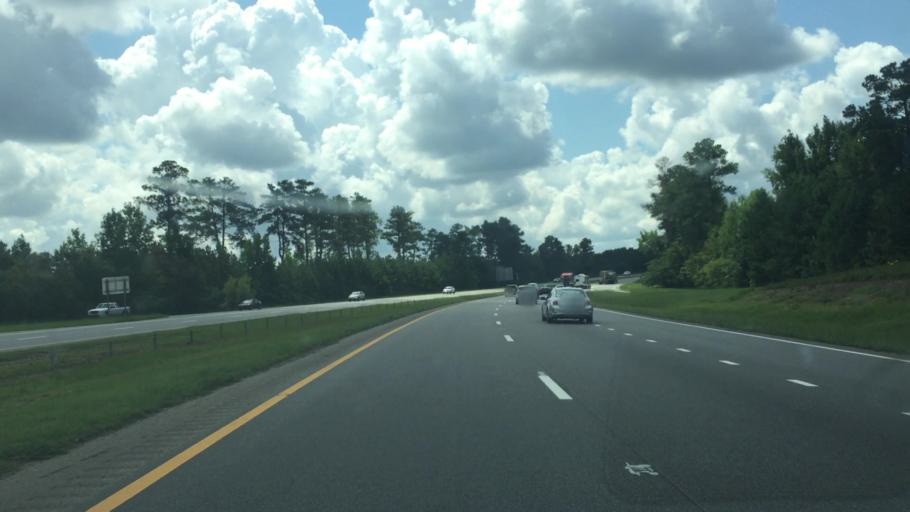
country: US
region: North Carolina
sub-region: Richmond County
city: East Rockingham
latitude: 34.9091
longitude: -79.7909
